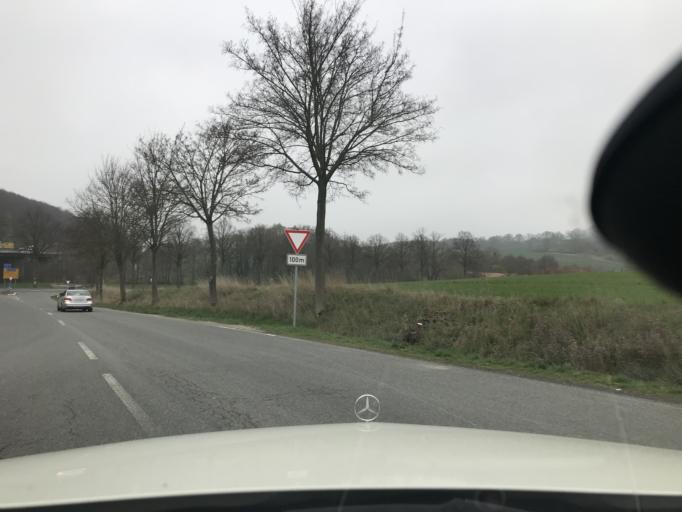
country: DE
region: Lower Saxony
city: Rosdorf
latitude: 51.4493
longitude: 9.8695
